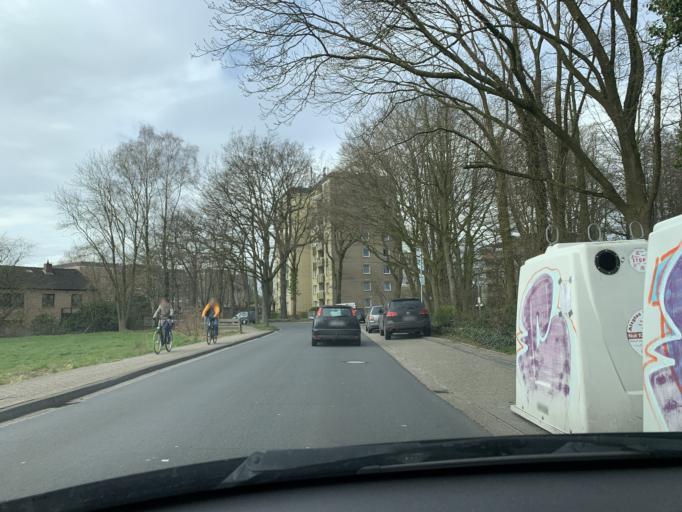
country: DE
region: Lower Saxony
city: Oldenburg
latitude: 53.1285
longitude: 8.1881
